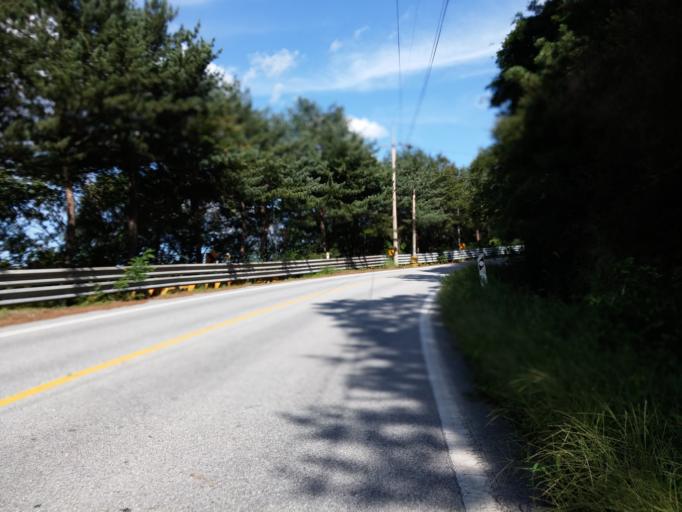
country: KR
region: Daejeon
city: Sintansin
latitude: 36.4940
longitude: 127.4850
